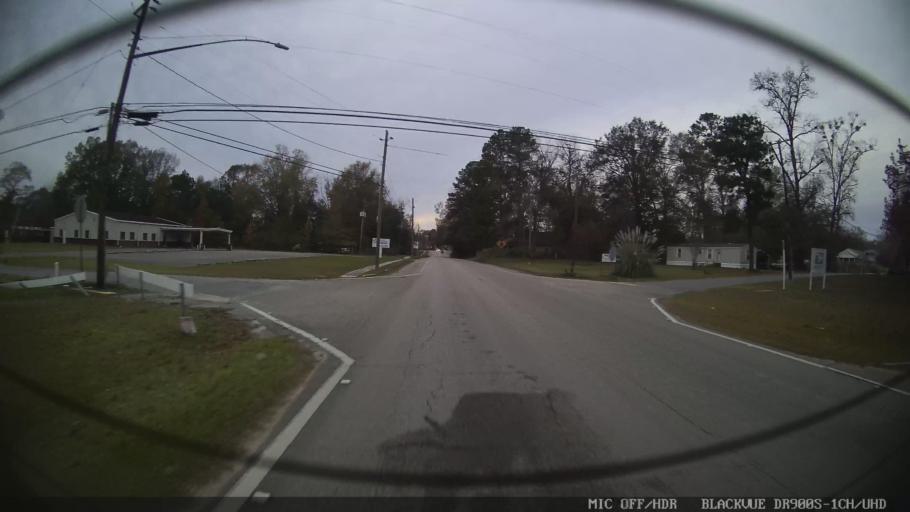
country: US
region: Mississippi
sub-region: Clarke County
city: Stonewall
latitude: 32.0394
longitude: -88.8817
